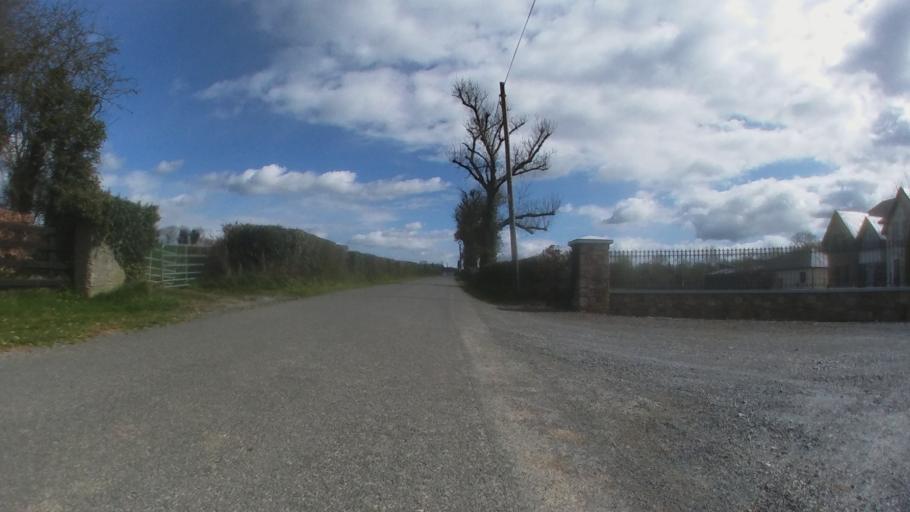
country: IE
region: Leinster
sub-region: Kilkenny
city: Kilkenny
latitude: 52.7158
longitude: -7.2295
